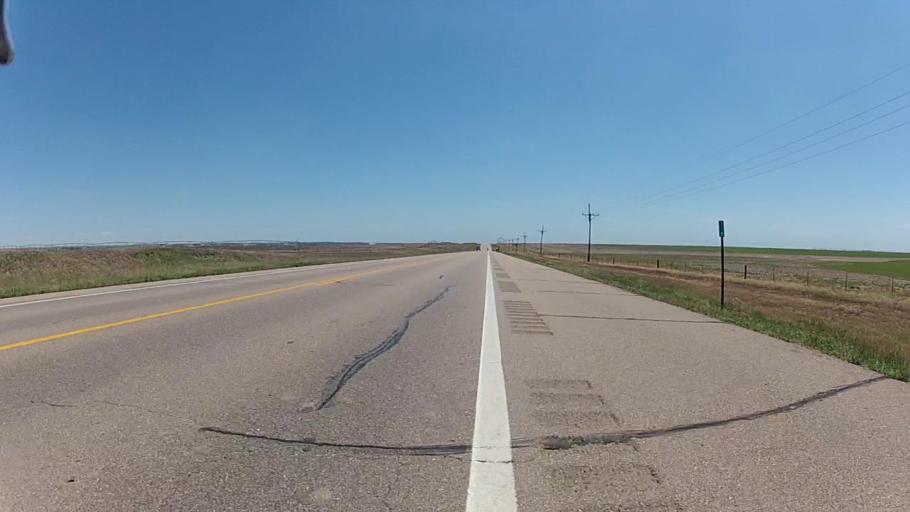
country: US
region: Kansas
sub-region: Ford County
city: Dodge City
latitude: 37.7144
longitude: -100.1014
